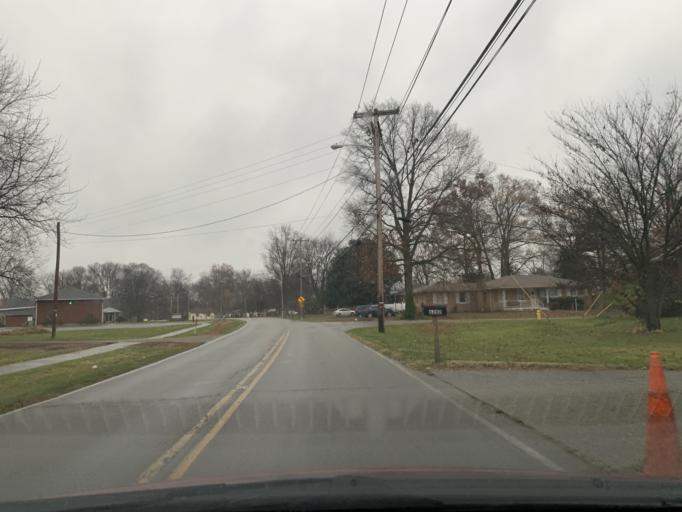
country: US
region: Kentucky
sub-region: Jefferson County
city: Buechel
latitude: 38.1988
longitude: -85.6425
